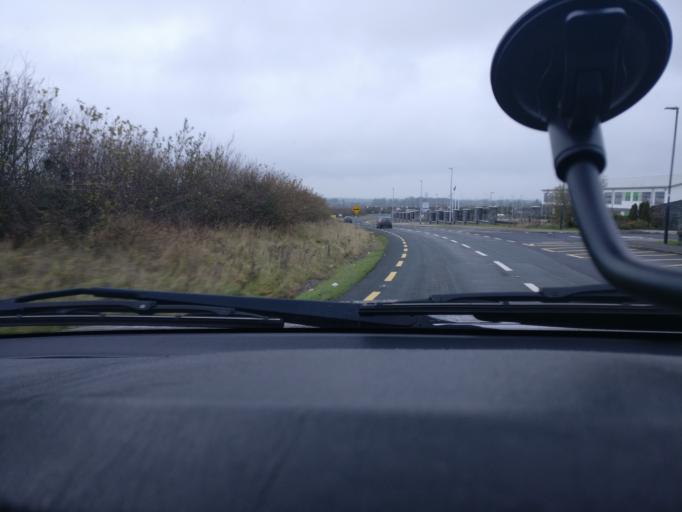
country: IE
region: Connaught
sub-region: County Galway
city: Loughrea
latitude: 53.2041
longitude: -8.5851
